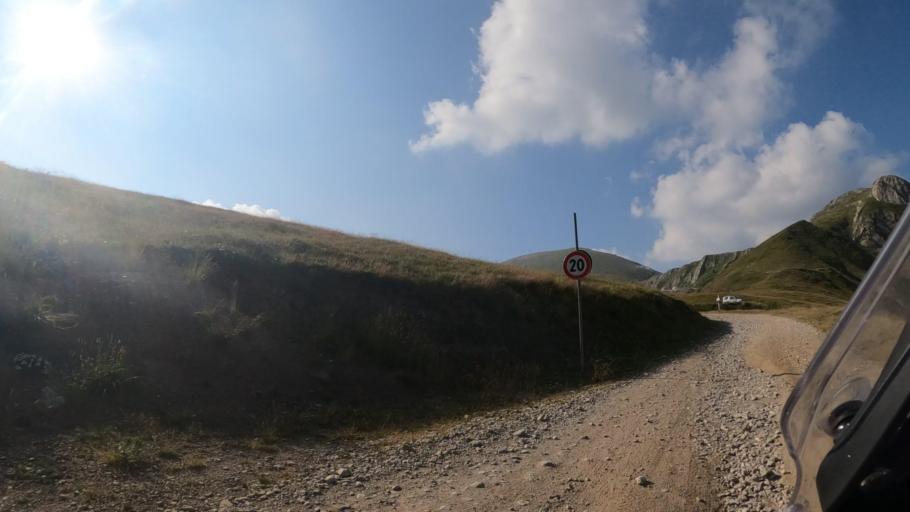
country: IT
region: Piedmont
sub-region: Provincia di Cuneo
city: Limone Piemonte
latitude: 44.1591
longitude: 7.6710
